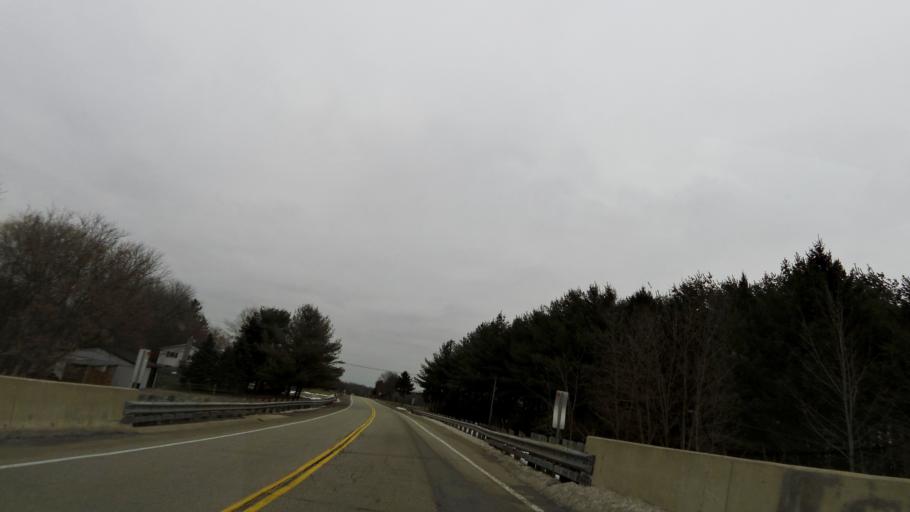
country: CA
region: Ontario
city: Brantford
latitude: 43.1102
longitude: -80.1346
